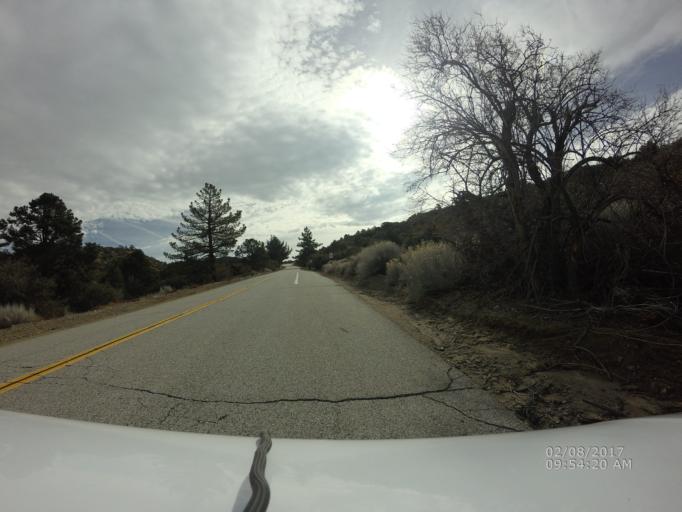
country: US
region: California
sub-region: San Bernardino County
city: Pinon Hills
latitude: 34.4212
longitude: -117.7966
